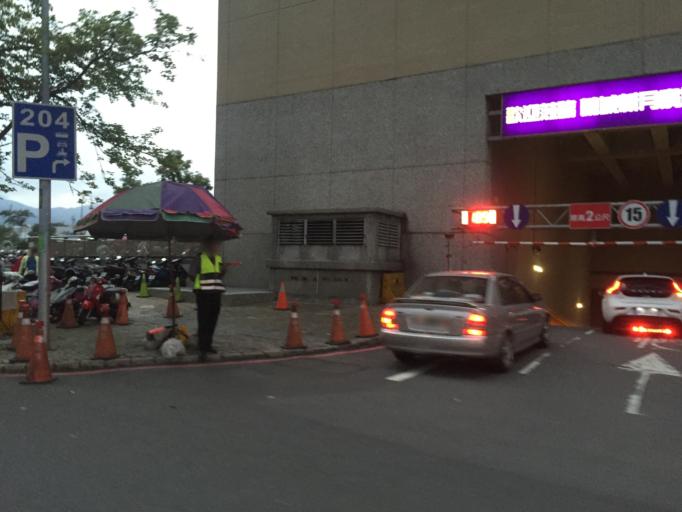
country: TW
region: Taiwan
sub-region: Yilan
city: Yilan
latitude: 24.7536
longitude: 121.7501
